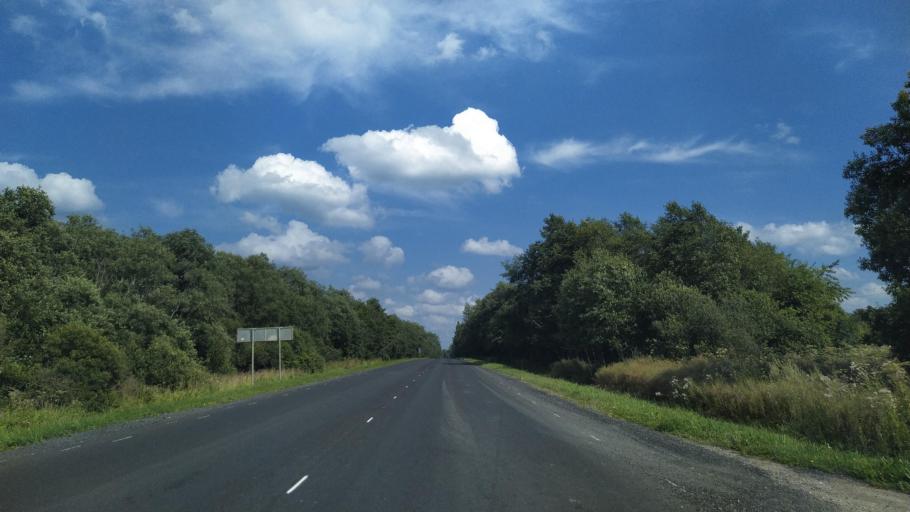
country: RU
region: Pskov
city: Porkhov
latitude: 57.7281
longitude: 29.3176
